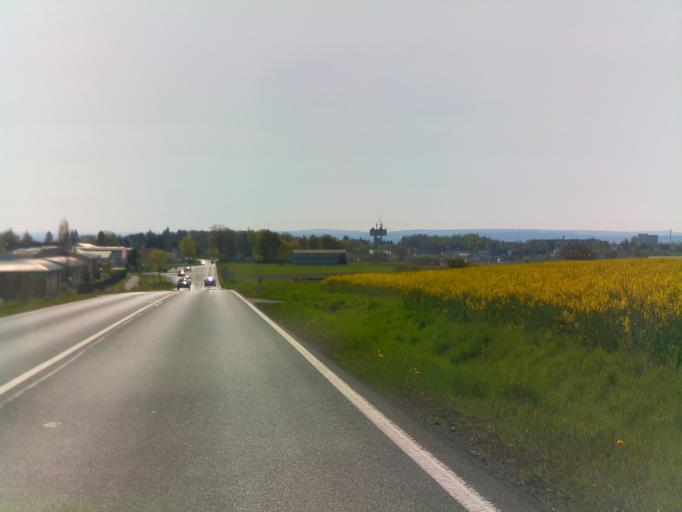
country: DE
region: Saxony
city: Syrau
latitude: 50.5382
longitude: 12.0915
